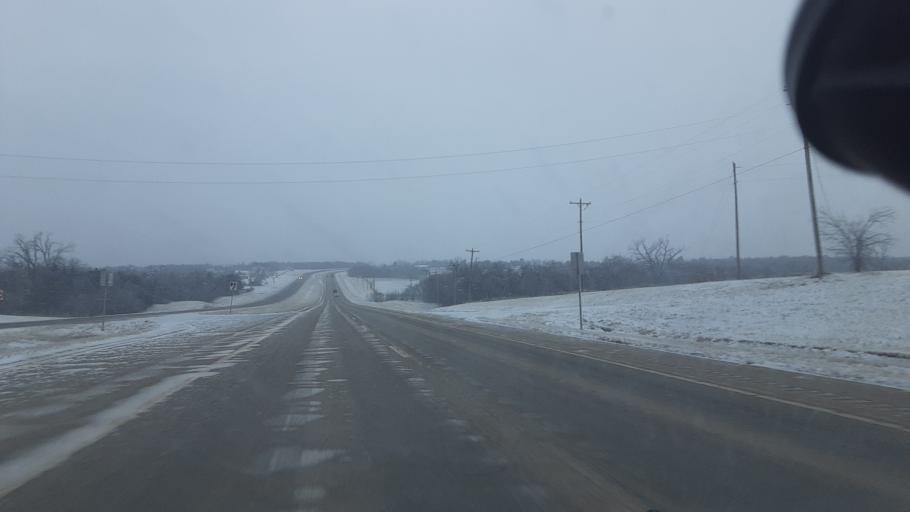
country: US
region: Oklahoma
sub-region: Logan County
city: Guthrie
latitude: 35.8921
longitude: -97.3634
